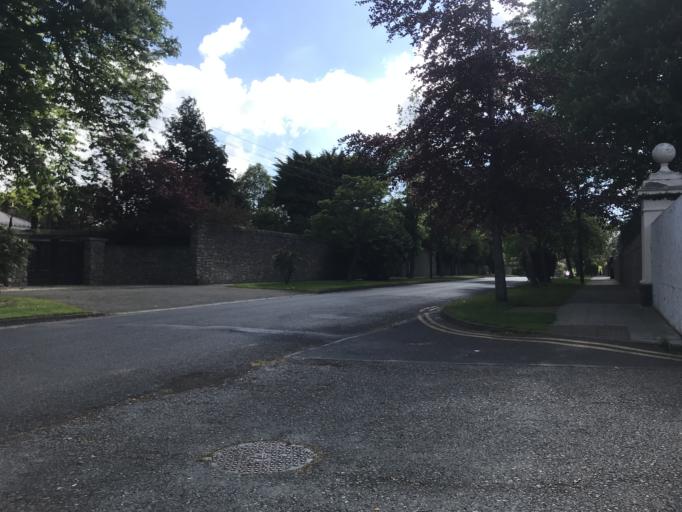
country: IE
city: Booterstown
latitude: 53.3028
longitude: -6.1965
